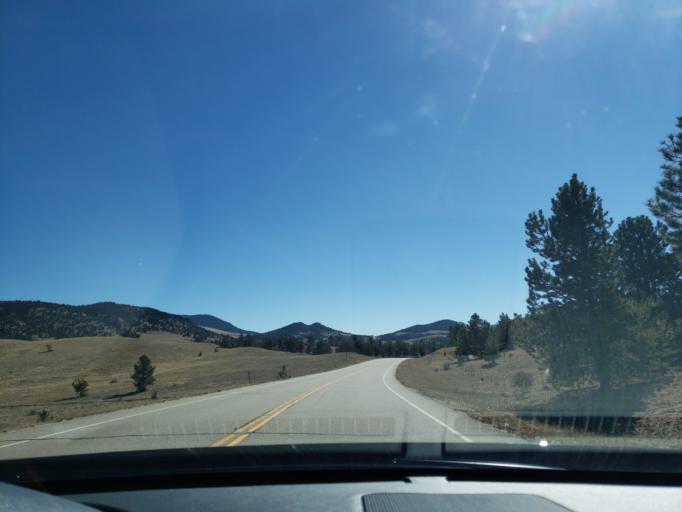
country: US
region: Colorado
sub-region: Chaffee County
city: Buena Vista
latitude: 38.8676
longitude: -105.6663
